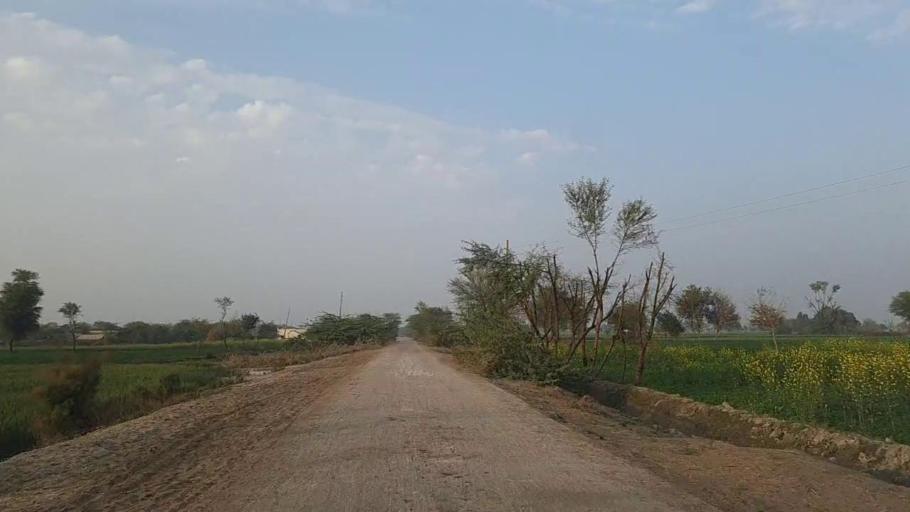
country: PK
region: Sindh
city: Jam Sahib
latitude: 26.3139
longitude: 68.6090
